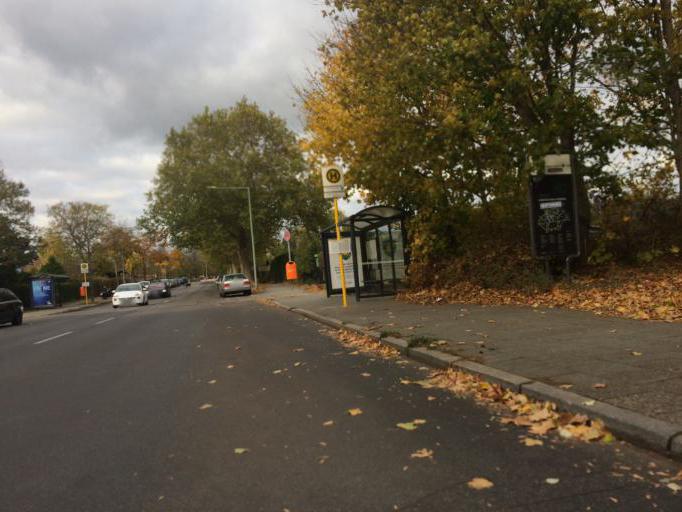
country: DE
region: Berlin
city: Lubars
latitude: 52.6065
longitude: 13.3489
